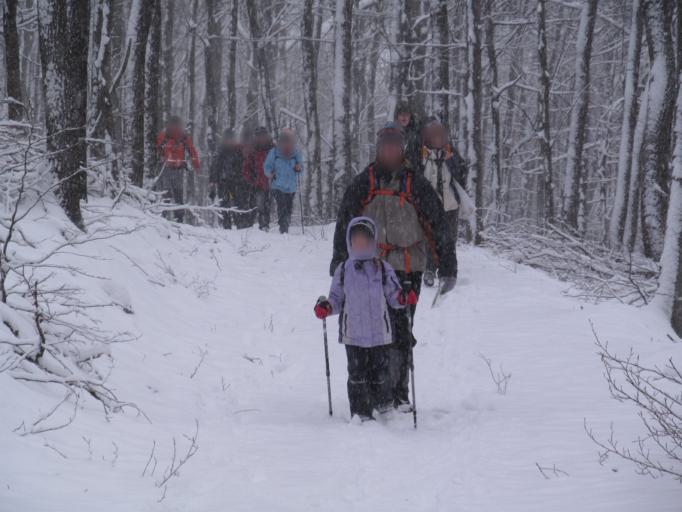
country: HU
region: Nograd
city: Diosjeno
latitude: 47.9540
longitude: 18.9820
